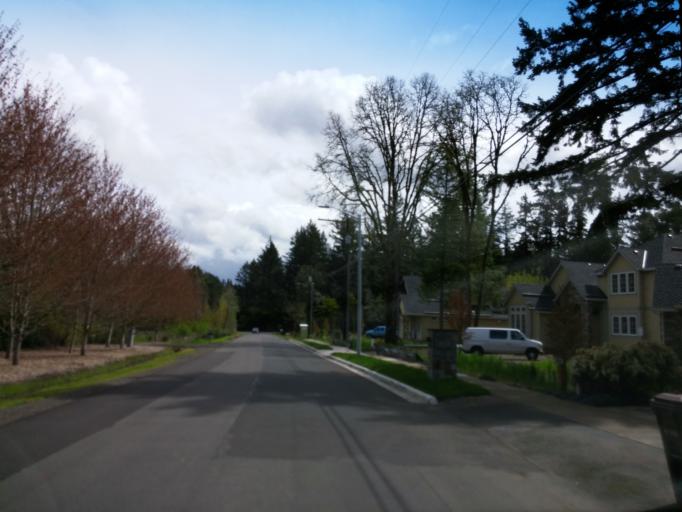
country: US
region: Oregon
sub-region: Washington County
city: Cedar Hills
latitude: 45.5026
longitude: -122.7967
